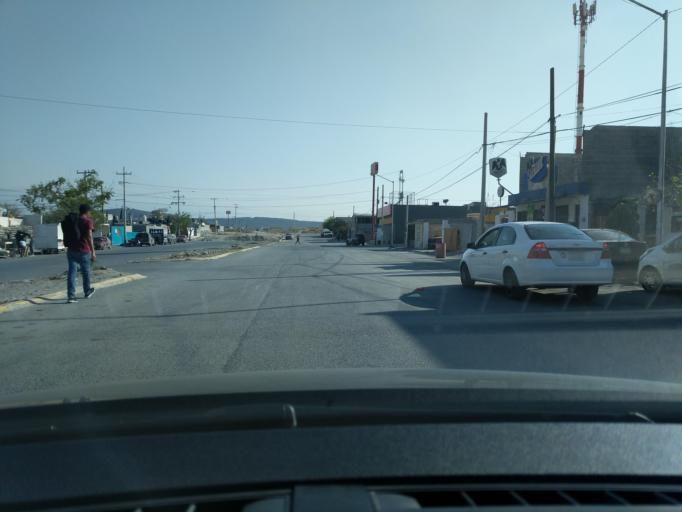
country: MX
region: Coahuila
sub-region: Ramos Arizpe
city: Ramos Arizpe
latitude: 25.5476
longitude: -100.9674
